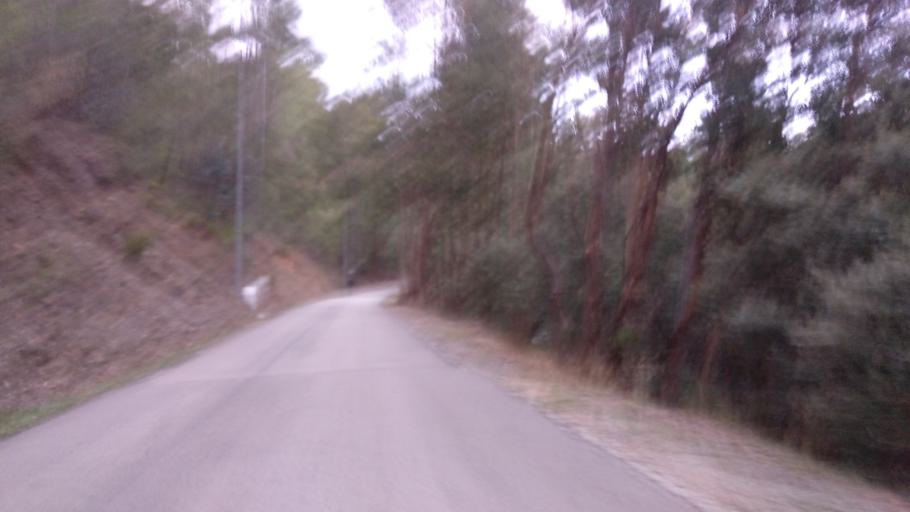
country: PT
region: Faro
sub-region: Sao Bras de Alportel
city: Sao Bras de Alportel
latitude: 37.1825
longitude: -7.9135
